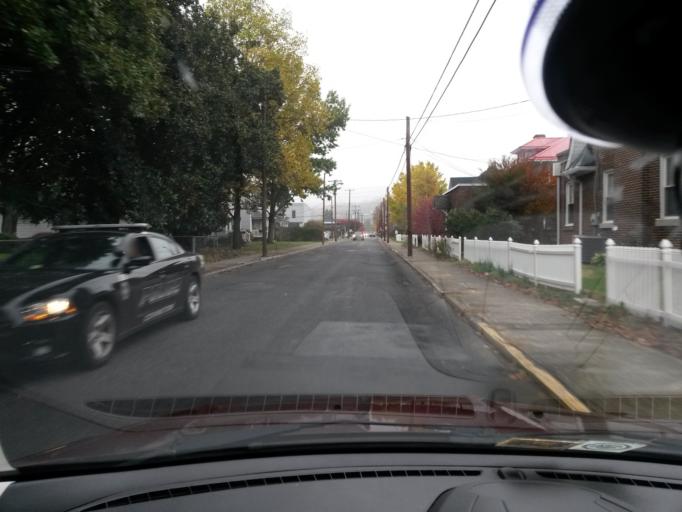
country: US
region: Virginia
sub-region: City of Covington
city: Covington
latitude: 37.7898
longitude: -79.9973
